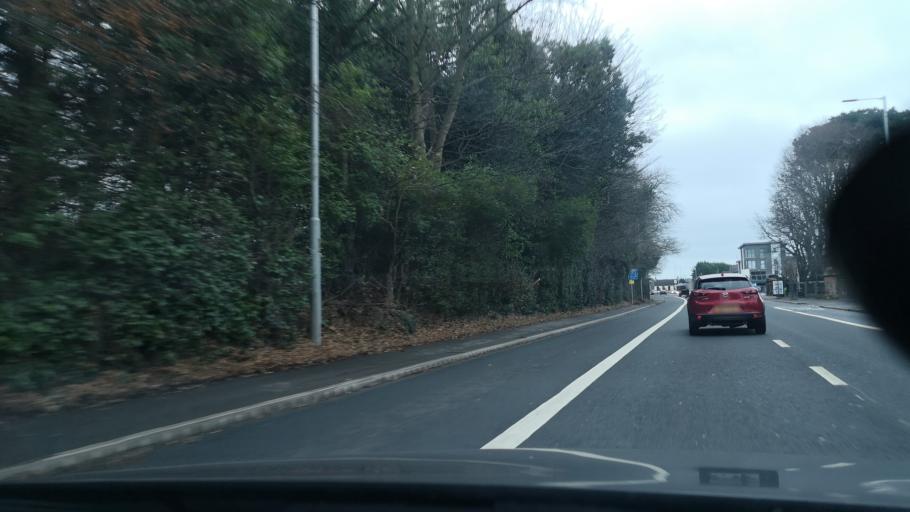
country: GB
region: Northern Ireland
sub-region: Castlereagh District
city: Dundonald
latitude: 54.5942
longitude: -5.8217
